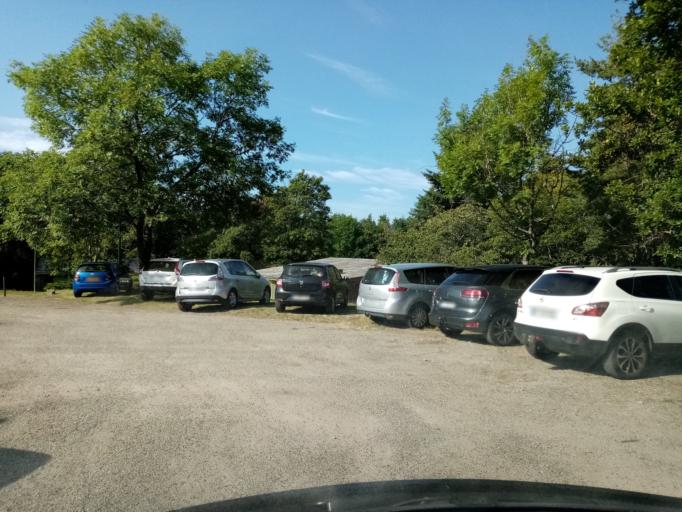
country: FR
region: Alsace
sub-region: Departement du Bas-Rhin
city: Ville
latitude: 48.3510
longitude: 7.3402
